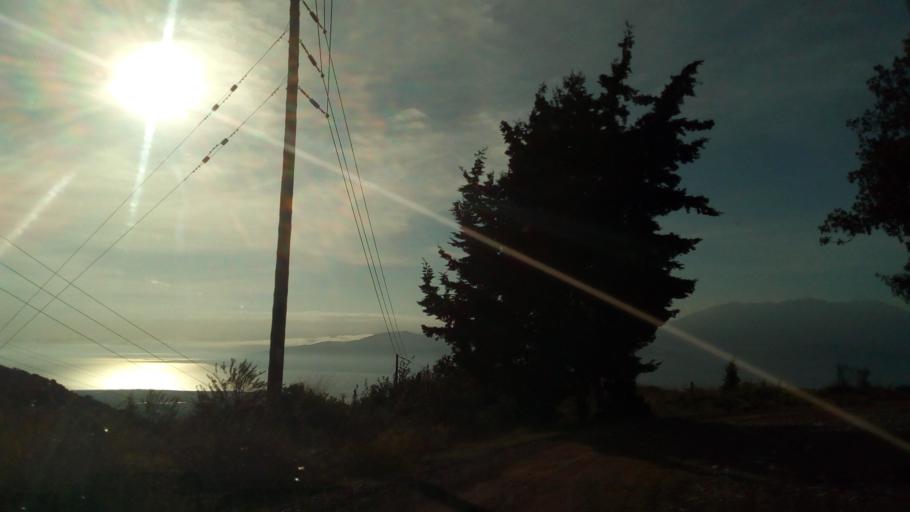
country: GR
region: West Greece
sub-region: Nomos Aitolias kai Akarnanias
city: Nafpaktos
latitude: 38.4087
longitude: 21.8201
